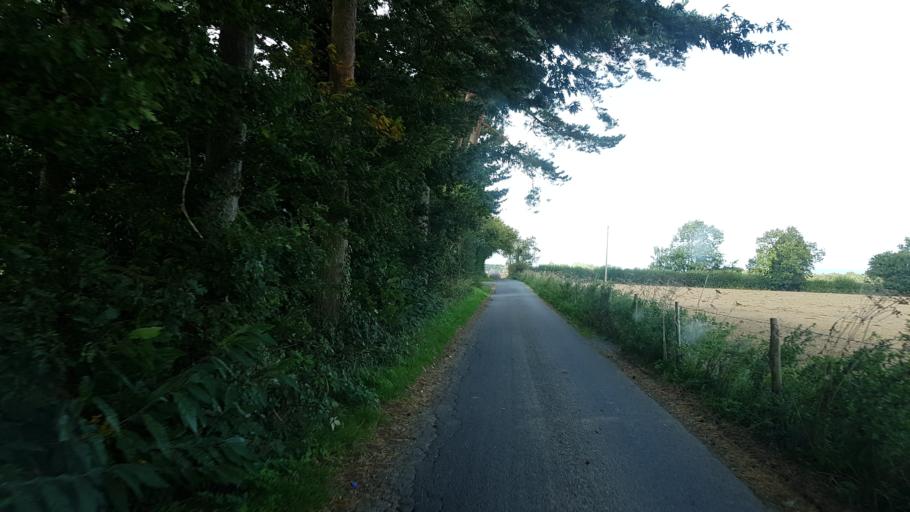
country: GB
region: England
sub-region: Kent
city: Harrietsham
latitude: 51.2399
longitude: 0.6184
